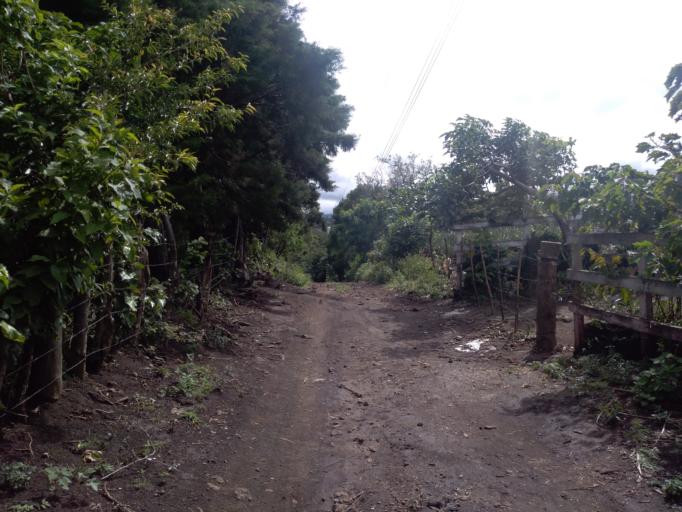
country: GT
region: Escuintla
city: San Vicente Pacaya
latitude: 14.3727
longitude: -90.5667
